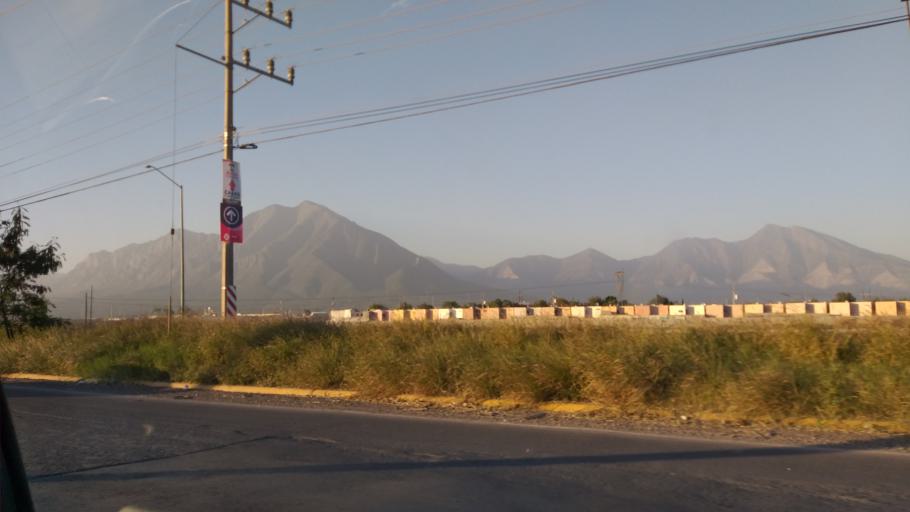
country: MX
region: Nuevo Leon
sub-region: Garcia
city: Mitras Poniente
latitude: 25.7765
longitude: -100.4384
